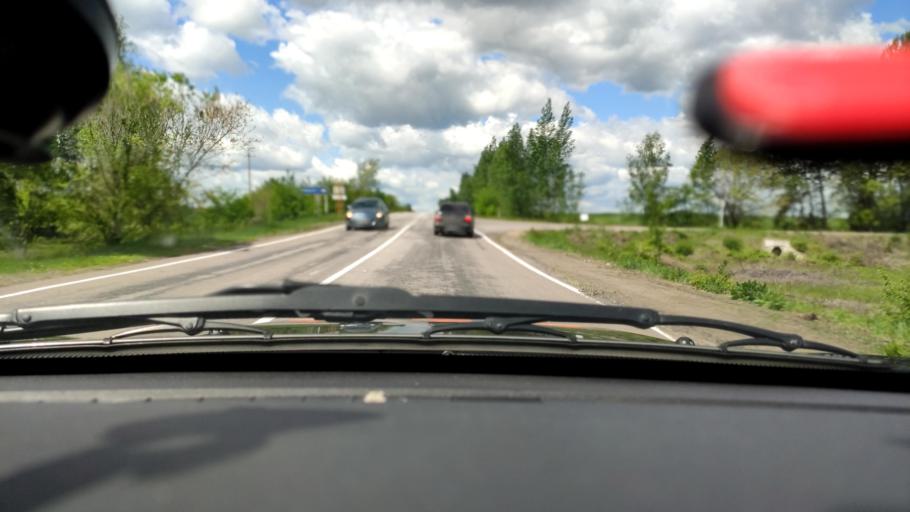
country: RU
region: Belgorod
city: Krasnoye
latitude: 51.0679
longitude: 38.8053
